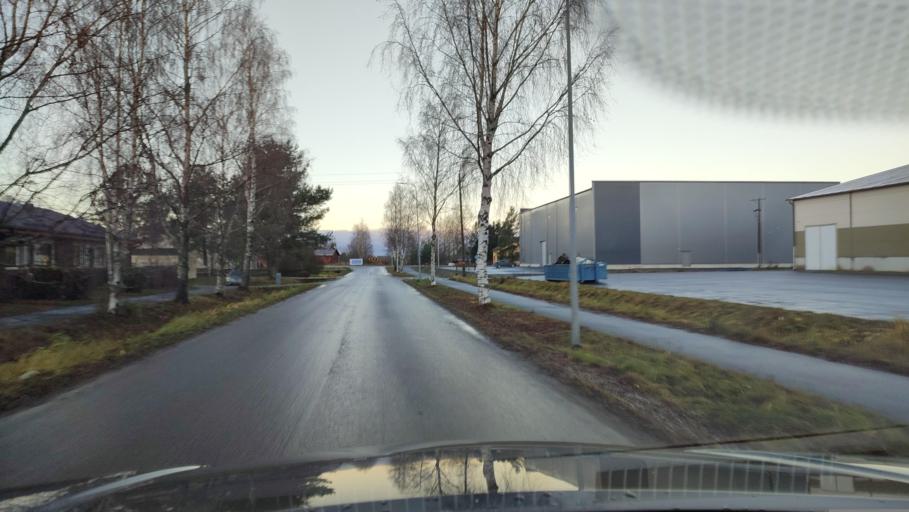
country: FI
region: Ostrobothnia
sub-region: Sydosterbotten
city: Naerpes
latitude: 62.4750
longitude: 21.3612
